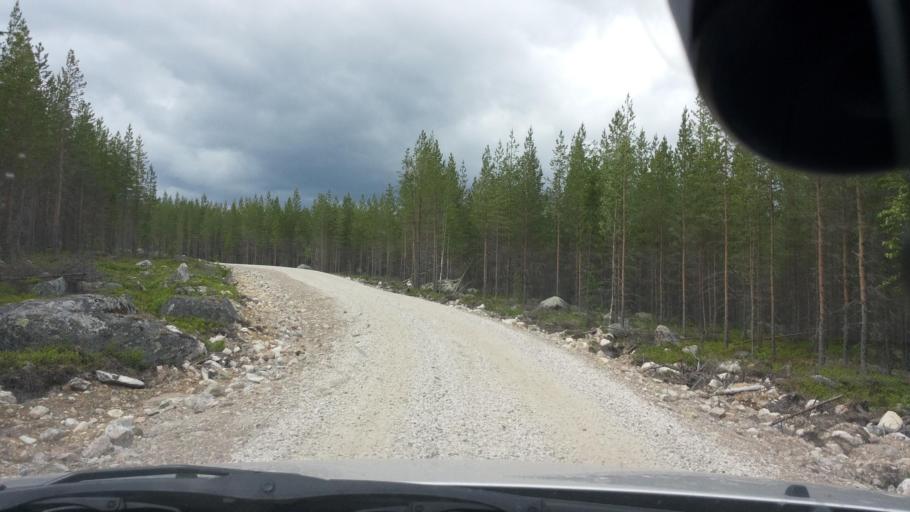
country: SE
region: Gaevleborg
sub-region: Ovanakers Kommun
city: Edsbyn
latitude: 61.4645
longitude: 15.2912
